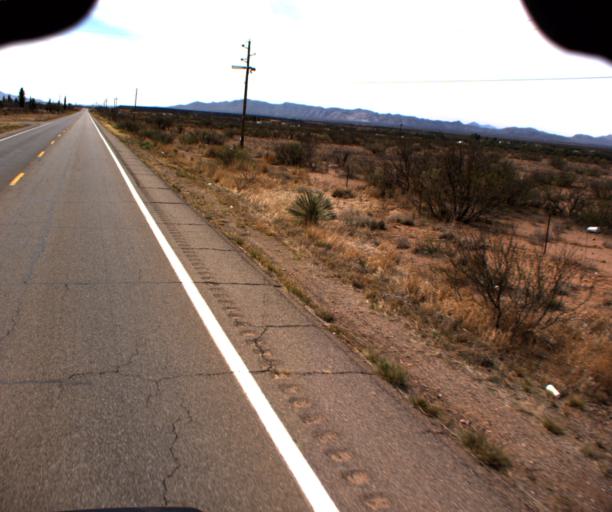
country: US
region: Arizona
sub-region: Cochise County
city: Pirtleville
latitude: 31.3684
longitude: -109.5794
